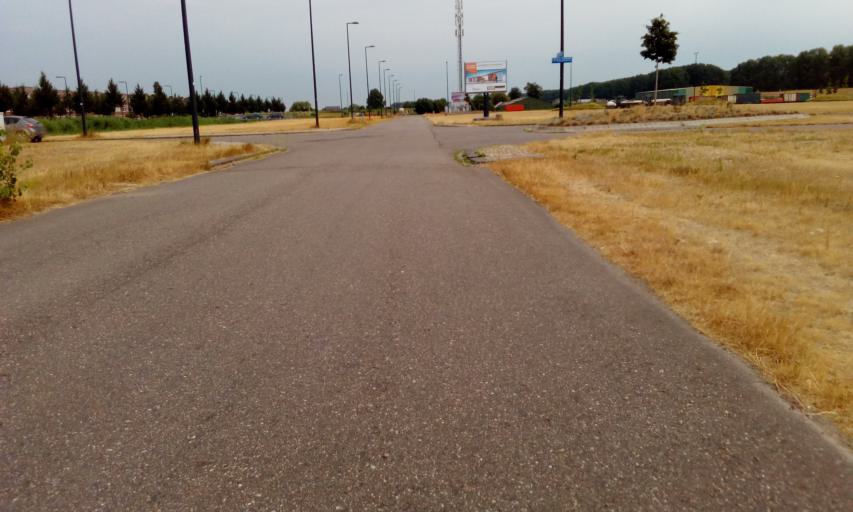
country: NL
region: South Holland
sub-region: Gemeente Capelle aan den IJssel
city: Capelle aan den IJssel
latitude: 51.9708
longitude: 4.5924
